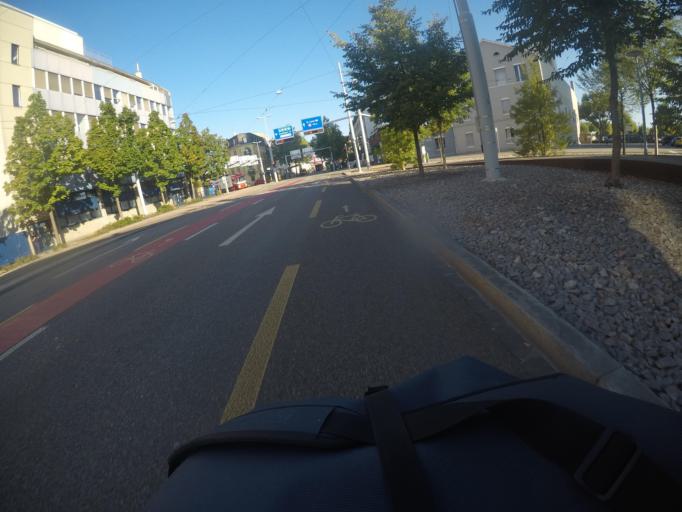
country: FR
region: Alsace
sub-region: Departement du Haut-Rhin
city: Village-Neuf
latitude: 47.5757
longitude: 7.5733
